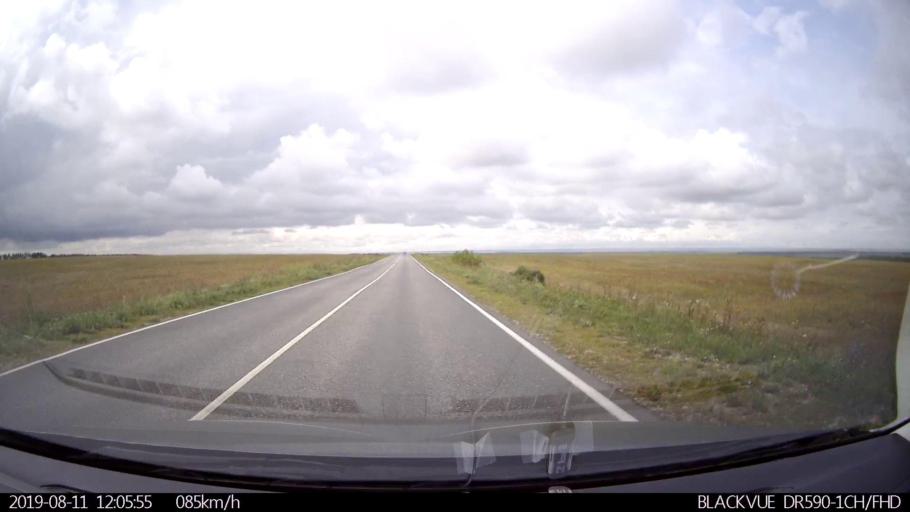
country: RU
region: Ulyanovsk
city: Silikatnyy
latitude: 53.9973
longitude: 48.1299
